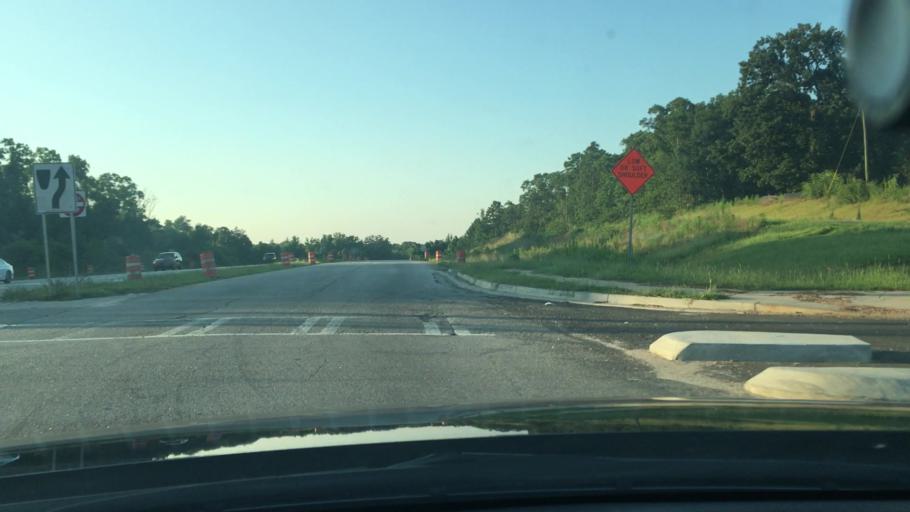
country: US
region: Georgia
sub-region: Coweta County
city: East Newnan
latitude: 33.3610
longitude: -84.7655
